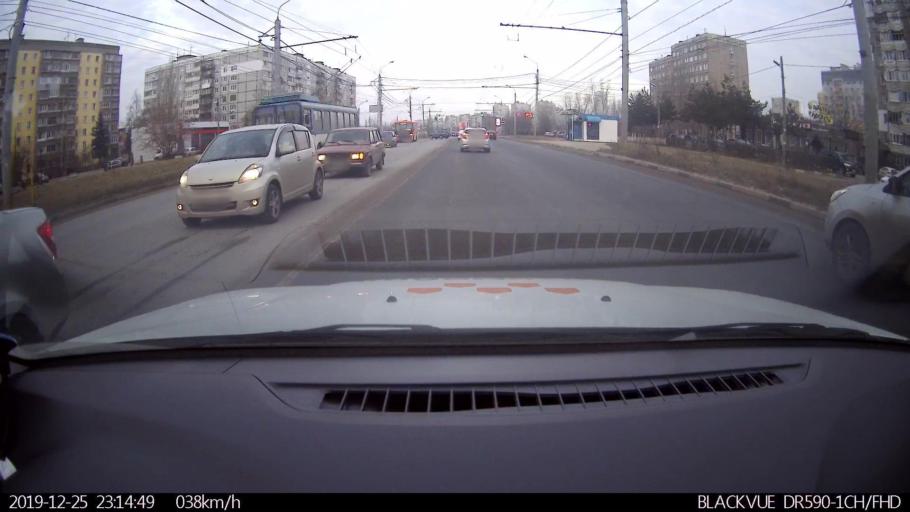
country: RU
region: Nizjnij Novgorod
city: Nizhniy Novgorod
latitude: 56.3355
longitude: 43.9203
